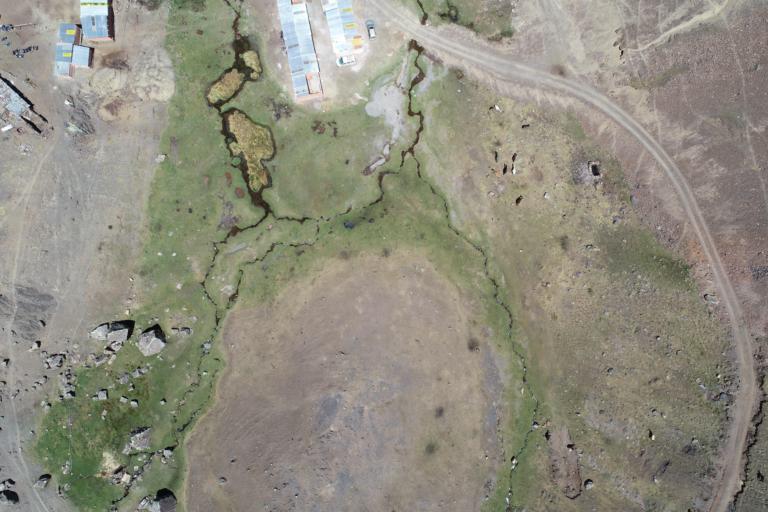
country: BO
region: La Paz
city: La Paz
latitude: -16.6205
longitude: -67.8277
